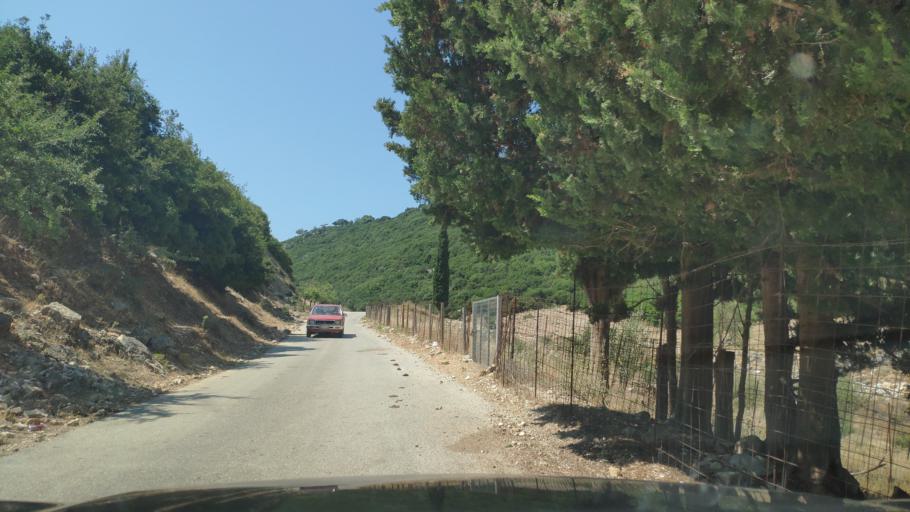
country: GR
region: West Greece
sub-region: Nomos Aitolias kai Akarnanias
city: Monastirakion
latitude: 38.8387
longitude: 20.9353
